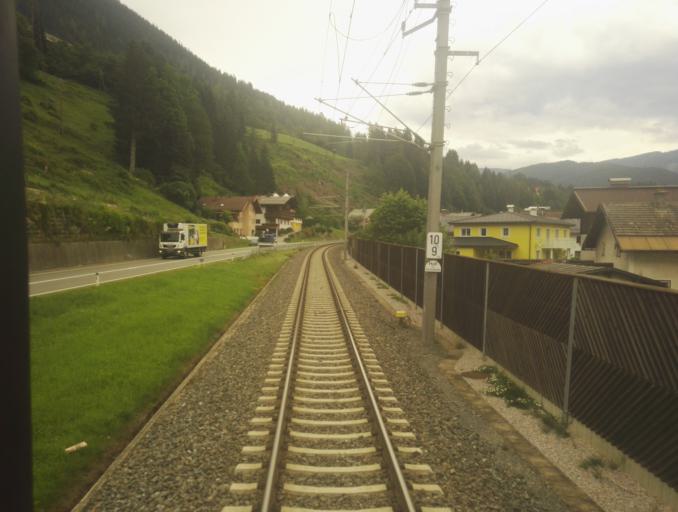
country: AT
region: Salzburg
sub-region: Politischer Bezirk Sankt Johann im Pongau
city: Huttau
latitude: 47.4203
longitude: 13.3291
